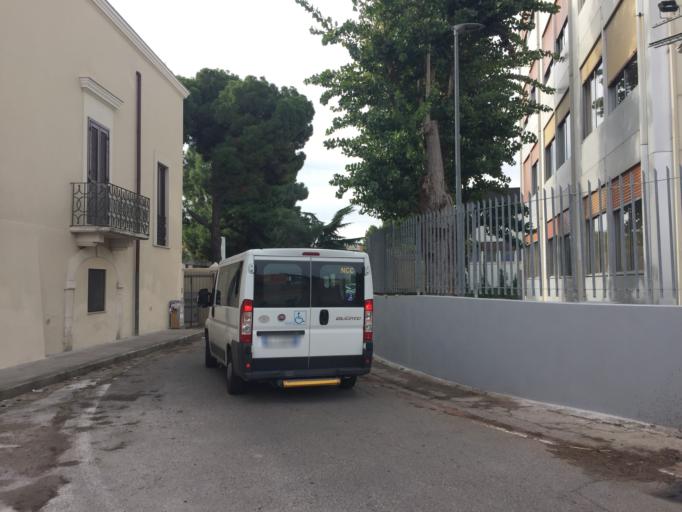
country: IT
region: Apulia
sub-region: Provincia di Bari
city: Bari
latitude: 41.1107
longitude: 16.8795
